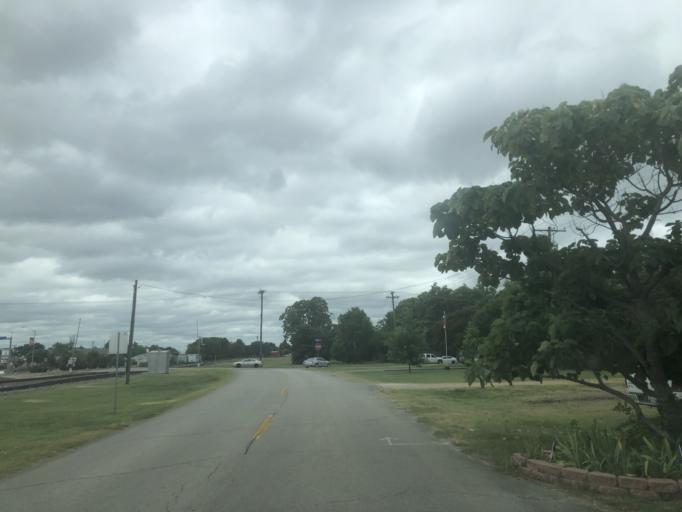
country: US
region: Texas
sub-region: Dallas County
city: Duncanville
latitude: 32.6555
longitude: -96.9085
